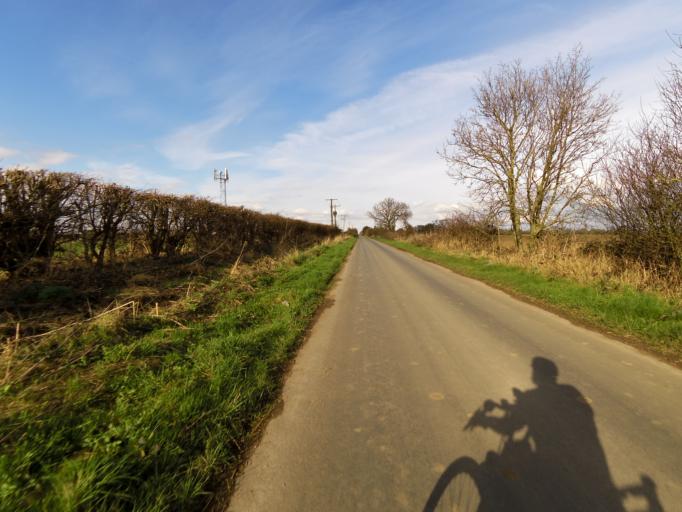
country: GB
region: England
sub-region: East Riding of Yorkshire
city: Pollington
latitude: 53.6843
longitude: -1.0652
